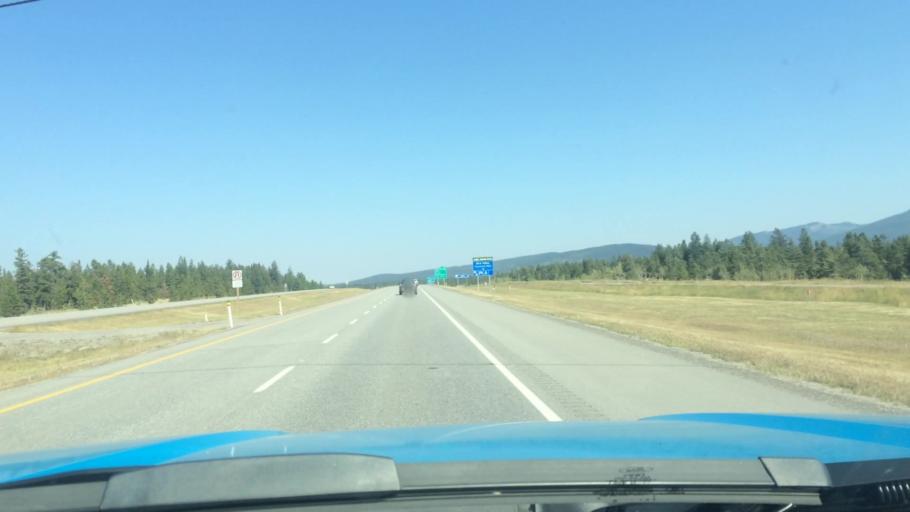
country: CA
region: Alberta
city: Canmore
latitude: 51.0713
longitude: -115.0732
